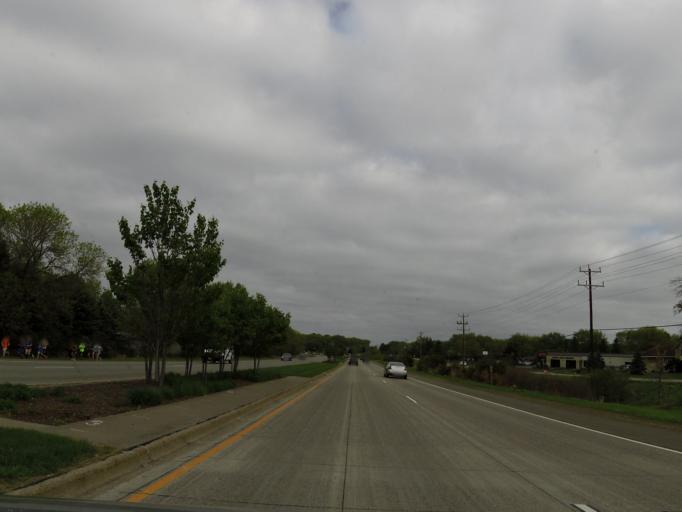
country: US
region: Minnesota
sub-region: Washington County
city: Woodbury
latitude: 44.9217
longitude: -92.9496
